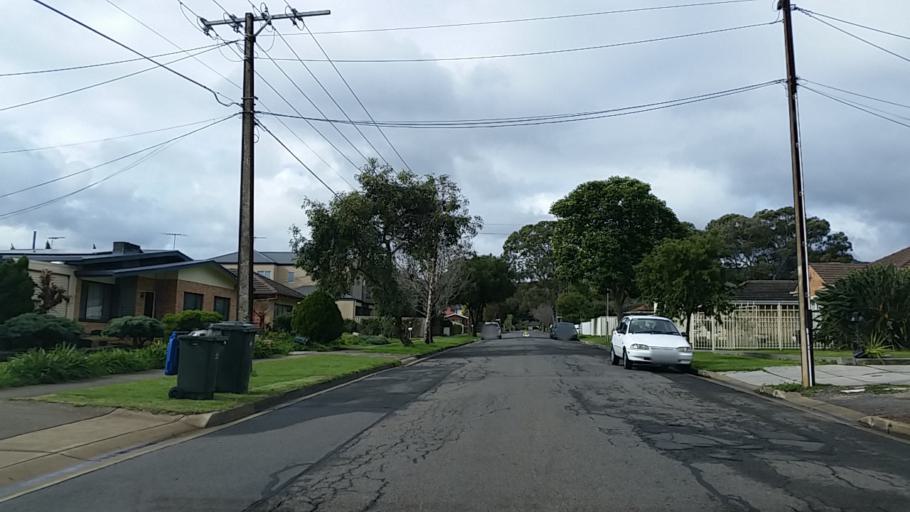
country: AU
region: South Australia
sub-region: Campbelltown
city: Campbelltown
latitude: -34.8922
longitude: 138.6777
